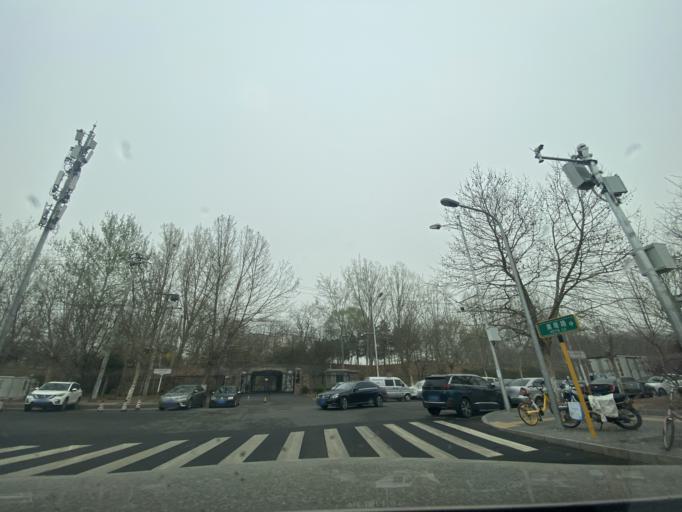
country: CN
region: Beijing
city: Sijiqing
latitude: 39.9581
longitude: 116.2287
